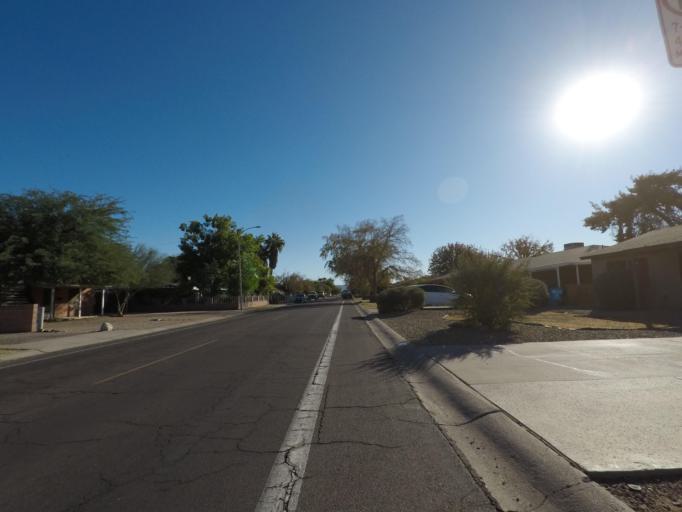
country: US
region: Arizona
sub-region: Maricopa County
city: Phoenix
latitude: 33.4892
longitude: -112.1085
